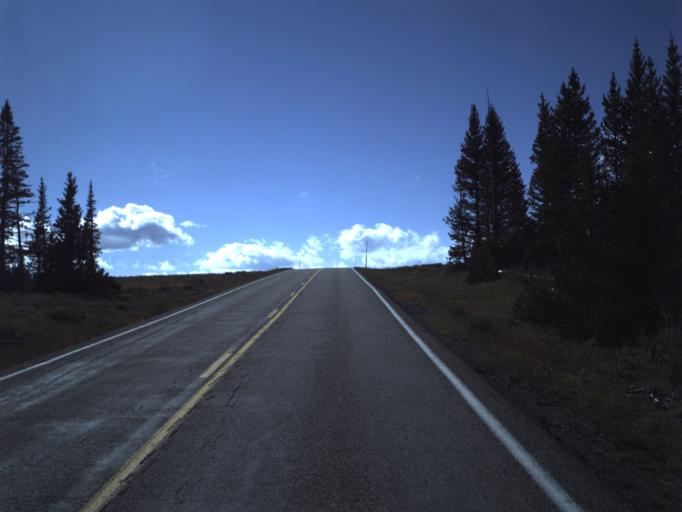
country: US
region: Utah
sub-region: Iron County
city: Parowan
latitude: 37.6546
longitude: -112.7666
